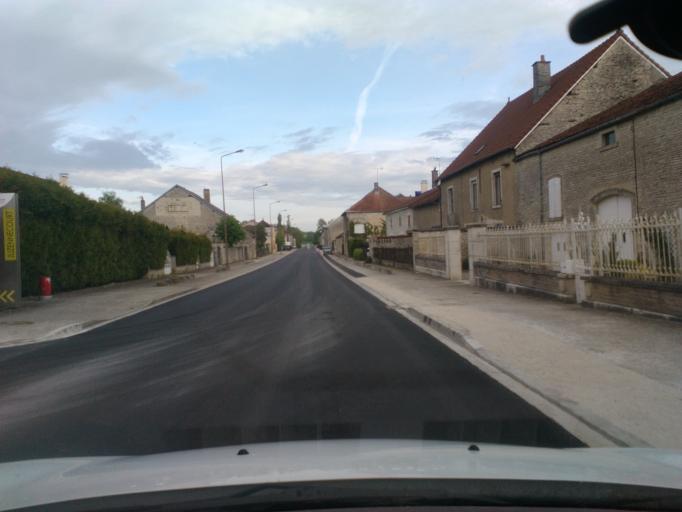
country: FR
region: Champagne-Ardenne
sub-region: Departement de la Haute-Marne
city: Lavilleneuve-au-Roi
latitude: 48.1822
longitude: 4.9810
